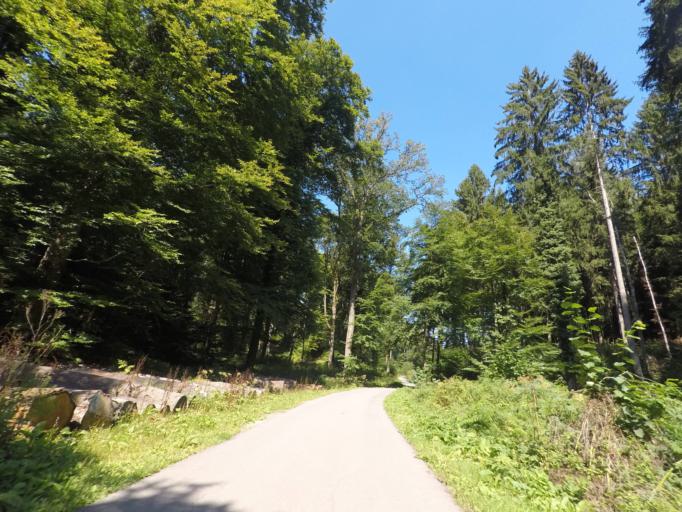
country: LU
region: Luxembourg
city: Bereldange
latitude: 49.6413
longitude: 6.1144
